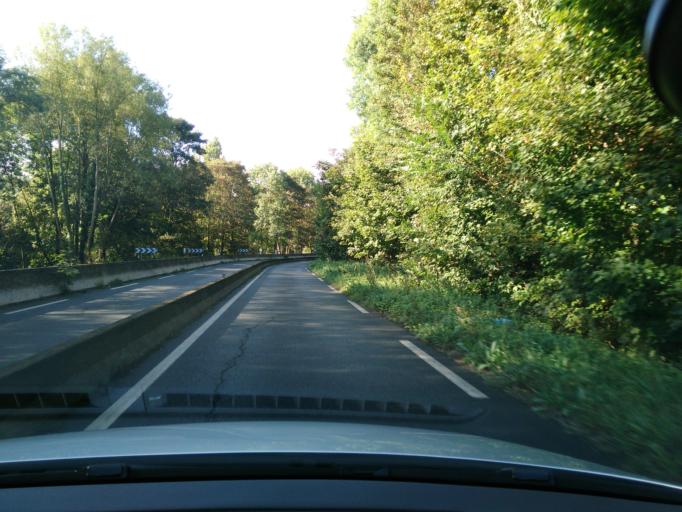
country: FR
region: Ile-de-France
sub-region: Departement de l'Essonne
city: Verrieres-le-Buisson
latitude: 48.7373
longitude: 2.2500
